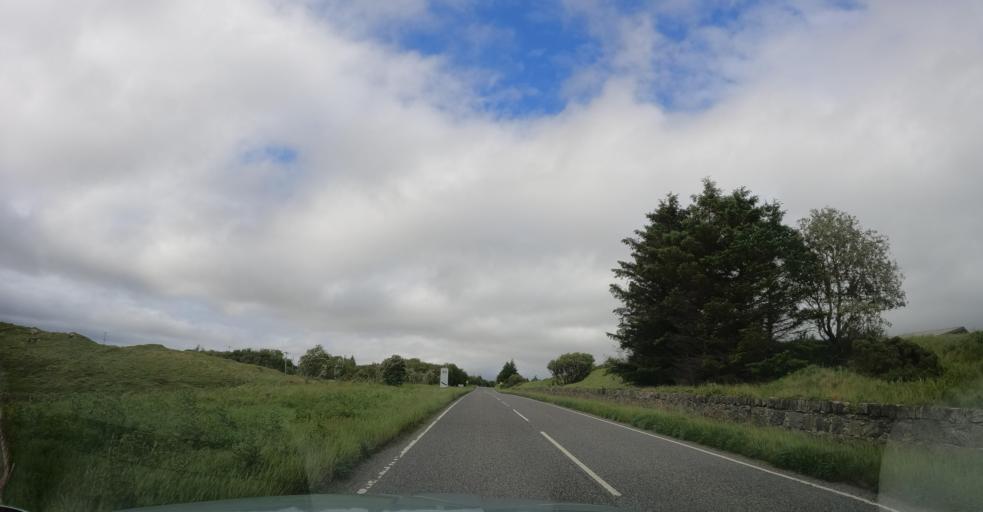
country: GB
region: Scotland
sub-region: Eilean Siar
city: Stornoway
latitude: 58.2092
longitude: -6.4182
